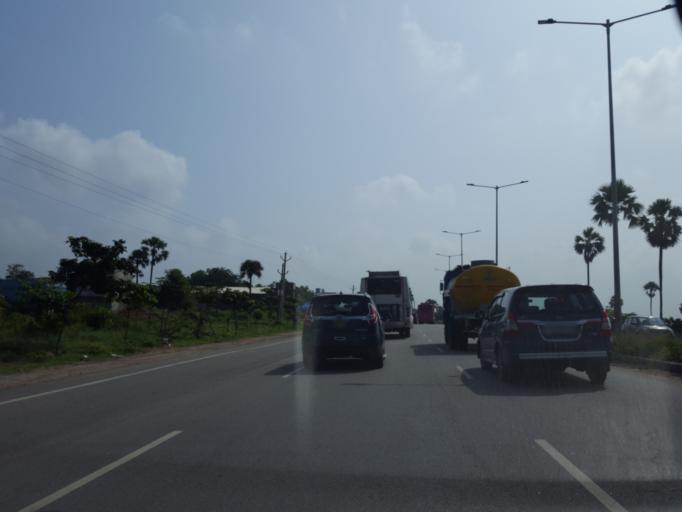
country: IN
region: Telangana
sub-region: Rangareddi
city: Ghatkesar
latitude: 17.3095
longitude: 78.6957
